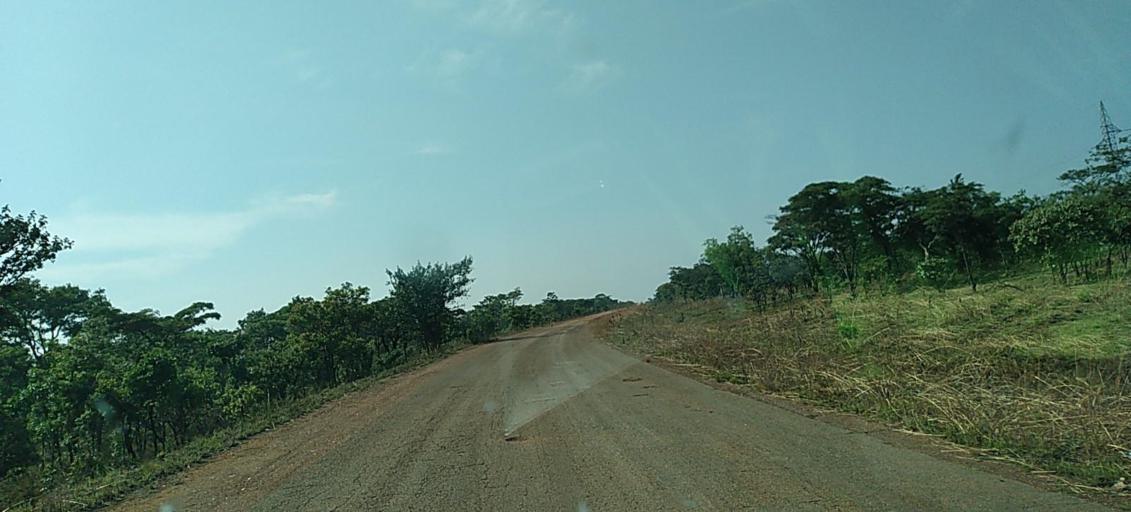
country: ZM
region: North-Western
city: Mwinilunga
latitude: -11.7931
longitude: 25.0712
